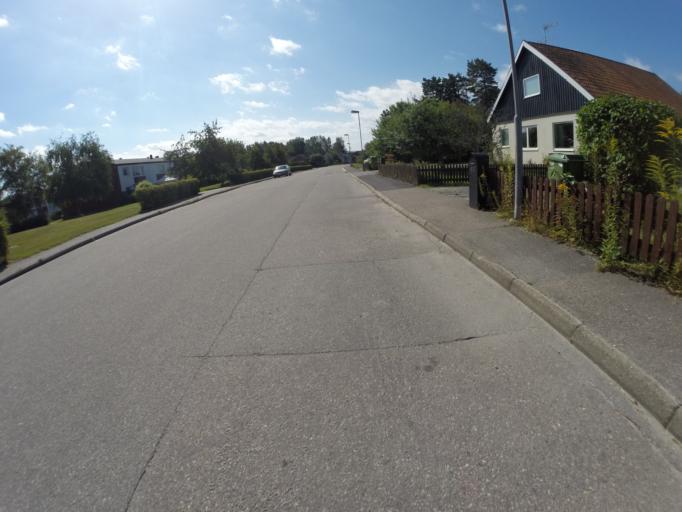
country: SE
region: Soedermanland
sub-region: Eskilstuna Kommun
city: Torshalla
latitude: 59.4148
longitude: 16.4896
